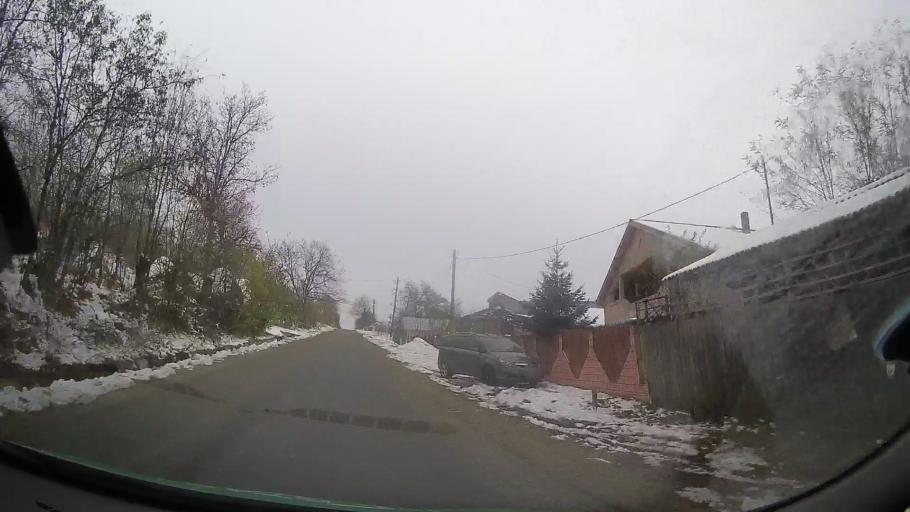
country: RO
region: Bacau
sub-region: Comuna Huruesti
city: Huruesti
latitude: 46.3055
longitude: 27.2939
